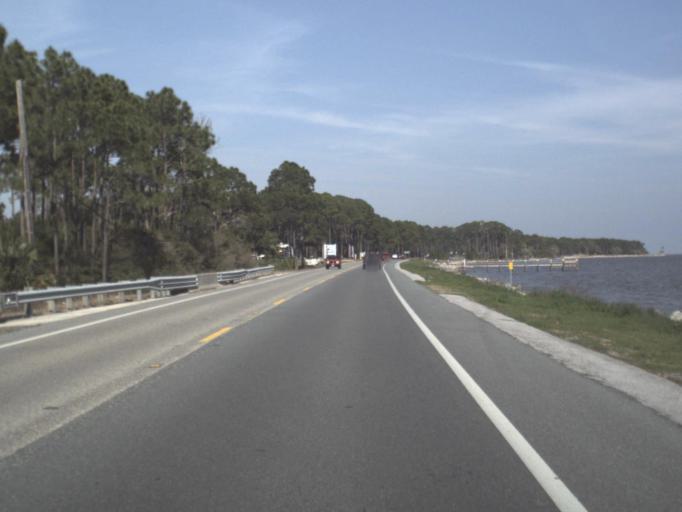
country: US
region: Florida
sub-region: Franklin County
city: Eastpoint
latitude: 29.7547
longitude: -84.8402
